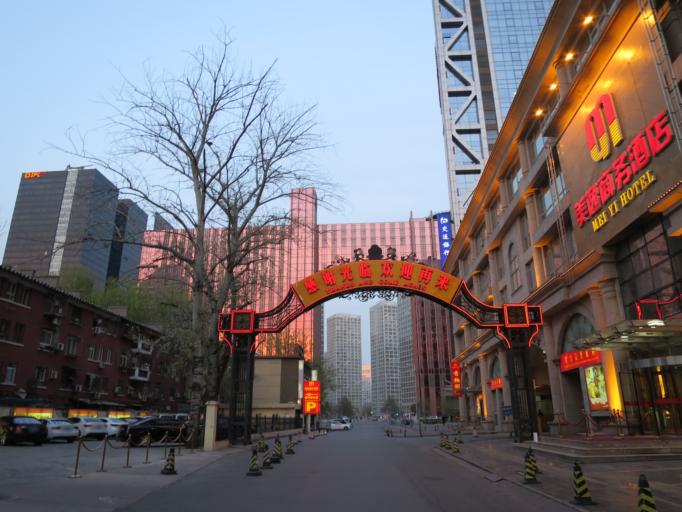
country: CN
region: Beijing
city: Chaowai
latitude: 39.9044
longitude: 116.4433
